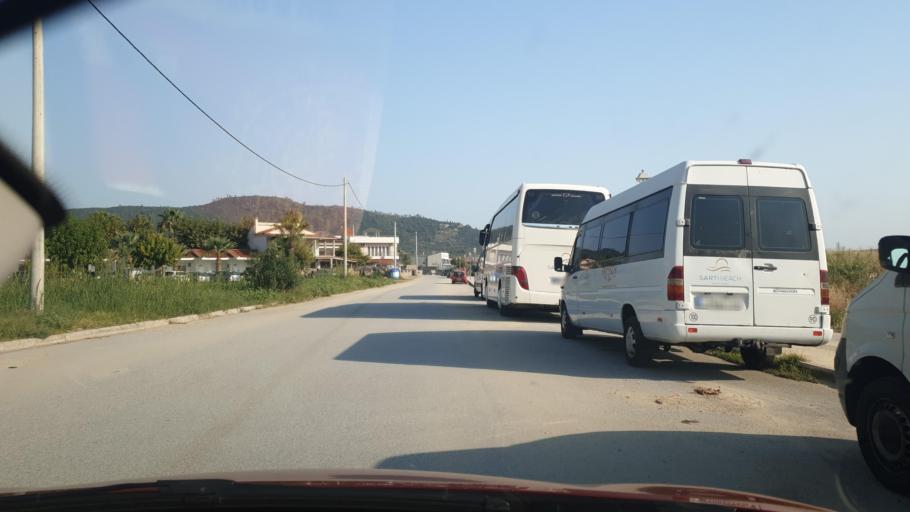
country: GR
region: Central Macedonia
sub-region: Nomos Chalkidikis
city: Sarti
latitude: 40.0833
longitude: 23.9790
